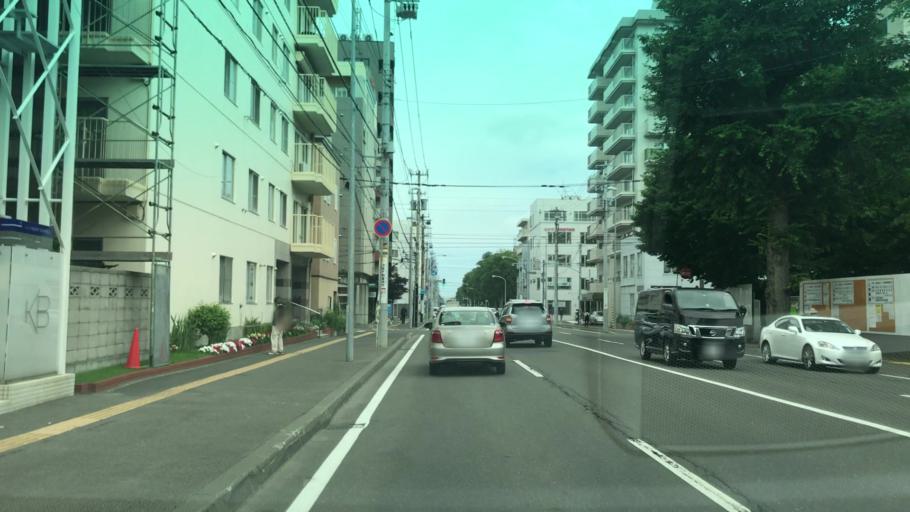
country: JP
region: Hokkaido
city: Sapporo
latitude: 43.0574
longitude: 141.3271
